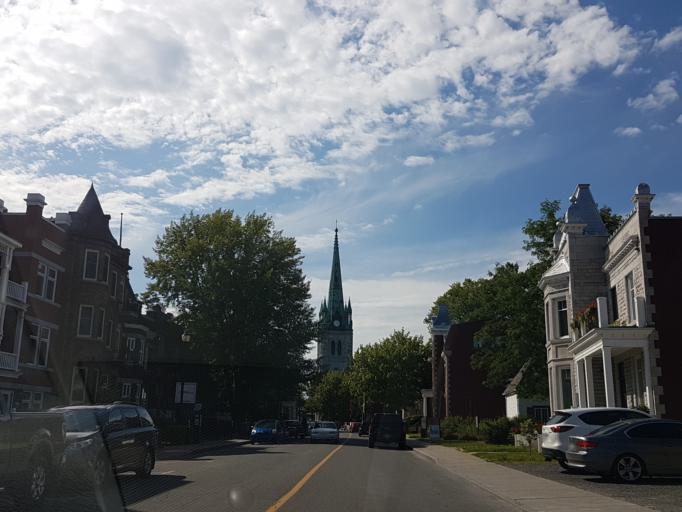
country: CA
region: Quebec
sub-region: Mauricie
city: Trois-Rivieres
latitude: 46.3432
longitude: -72.5400
